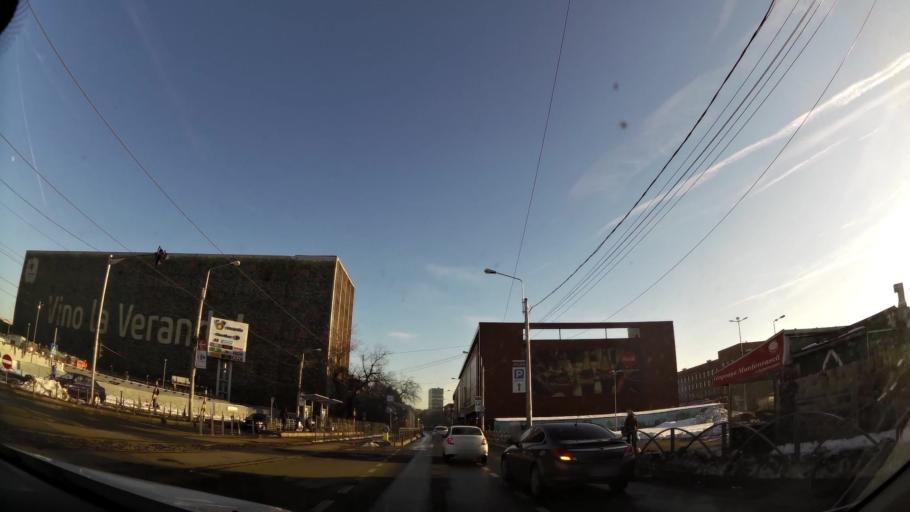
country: RO
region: Bucuresti
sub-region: Municipiul Bucuresti
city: Bucharest
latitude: 44.4512
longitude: 26.1295
